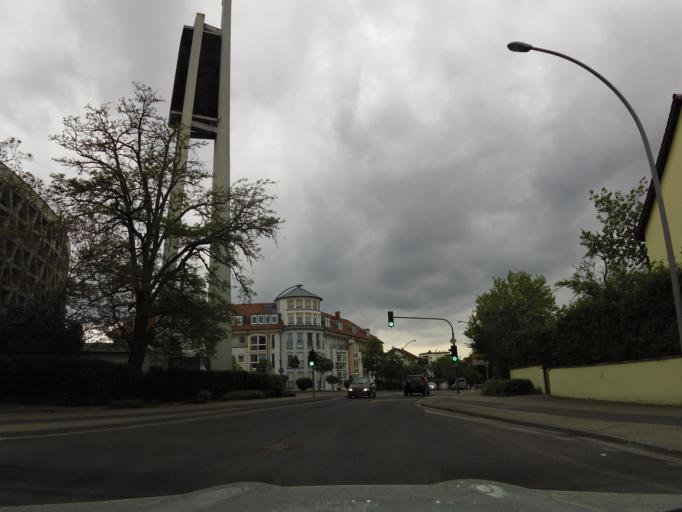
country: DE
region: Hesse
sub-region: Regierungsbezirk Darmstadt
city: Russelsheim
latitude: 49.9969
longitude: 8.4370
